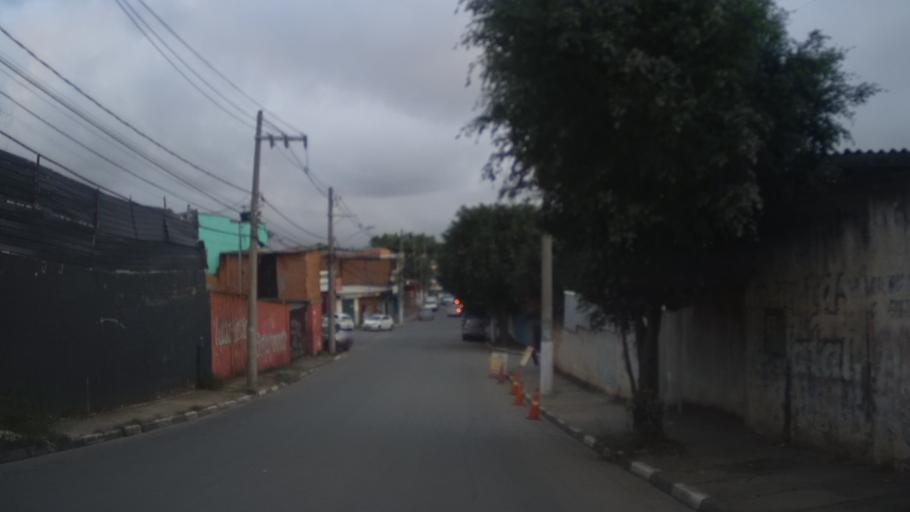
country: BR
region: Sao Paulo
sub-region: Guarulhos
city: Guarulhos
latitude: -23.4605
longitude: -46.4418
